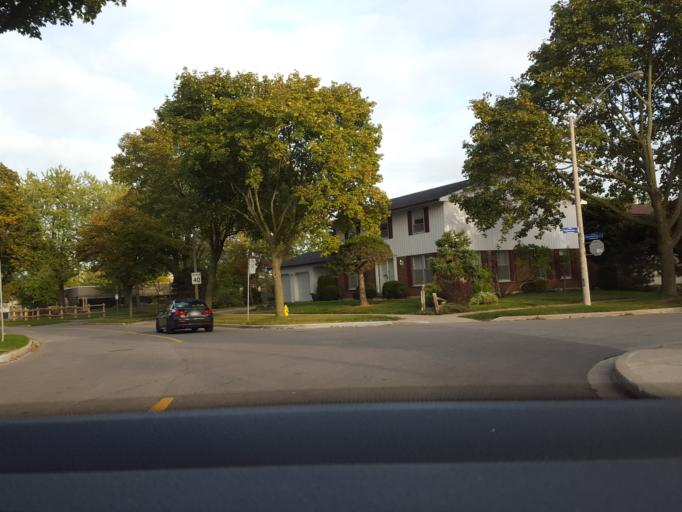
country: CA
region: Ontario
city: Scarborough
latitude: 43.7852
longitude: -79.3051
